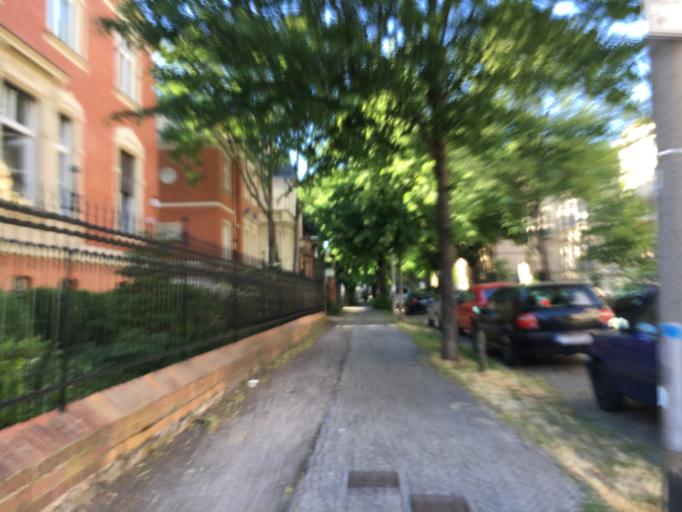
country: DE
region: Brandenburg
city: Potsdam
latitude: 52.4052
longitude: 13.0620
